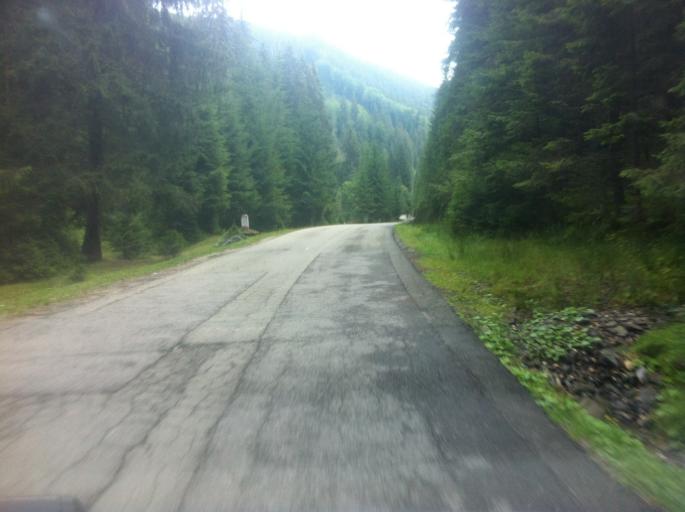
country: RO
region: Hunedoara
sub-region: Oras Petrila
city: Petrila
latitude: 45.4109
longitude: 23.5418
